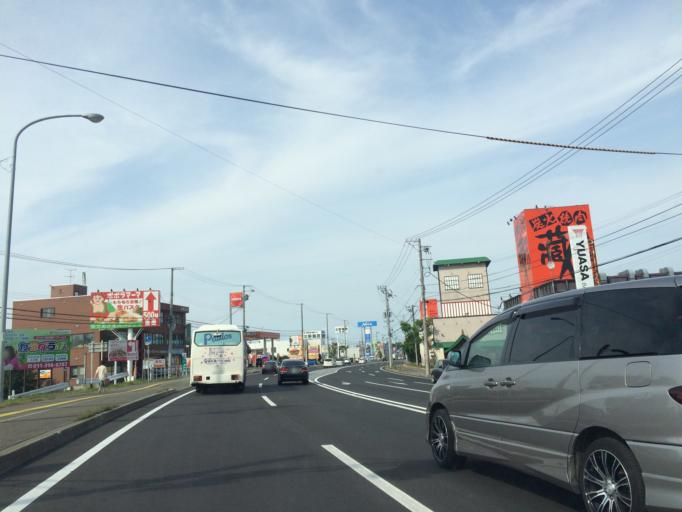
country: JP
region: Hokkaido
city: Ebetsu
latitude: 43.0874
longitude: 141.5159
